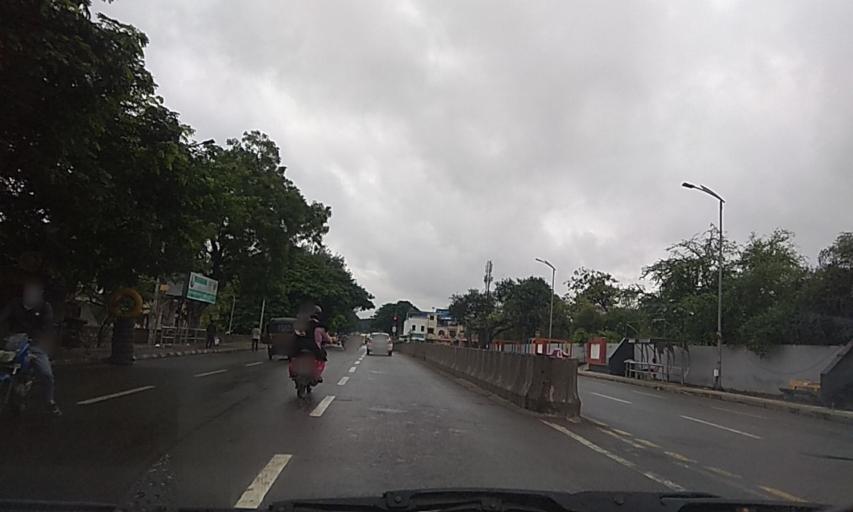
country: IN
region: Maharashtra
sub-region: Pune Division
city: Khadki
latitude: 18.5525
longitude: 73.8737
